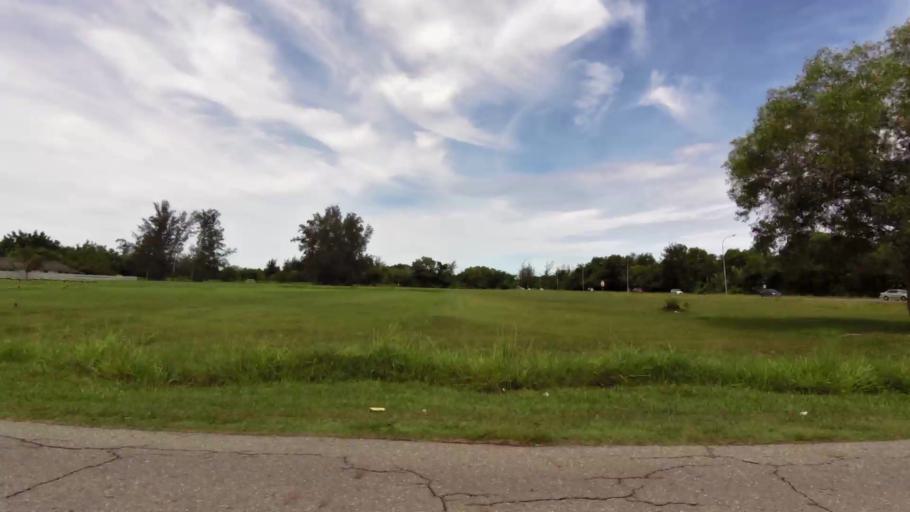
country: BN
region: Belait
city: Seria
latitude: 4.6078
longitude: 114.3080
